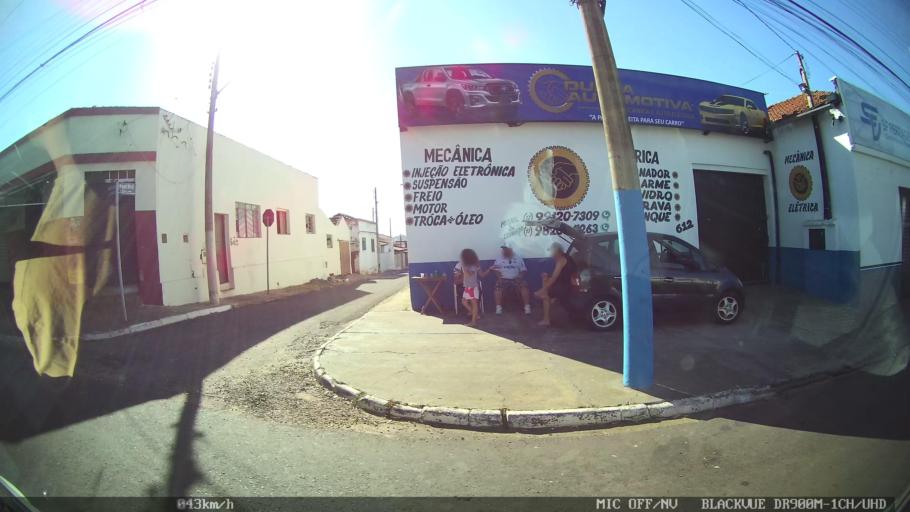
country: BR
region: Sao Paulo
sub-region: Olimpia
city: Olimpia
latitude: -20.7445
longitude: -48.9081
